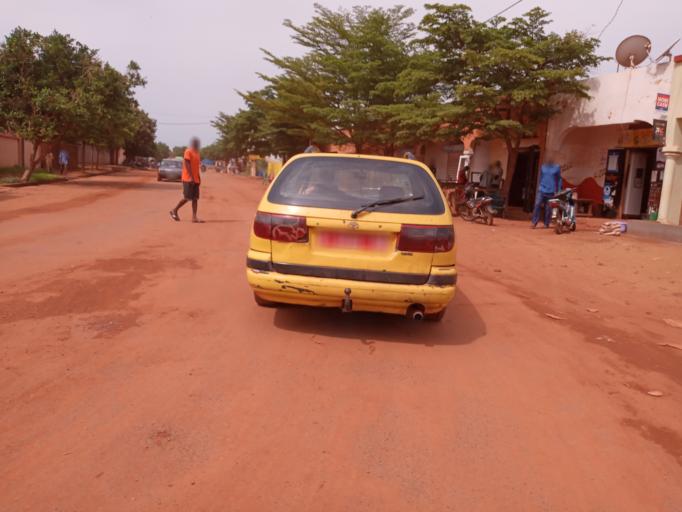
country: ML
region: Bamako
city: Bamako
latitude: 12.5534
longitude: -7.9989
